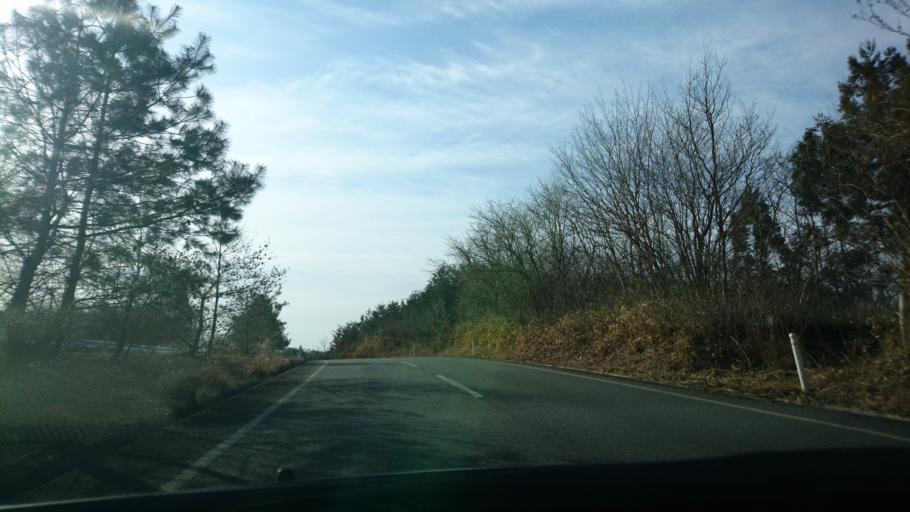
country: JP
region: Iwate
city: Ichinoseki
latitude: 38.8561
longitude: 141.2010
